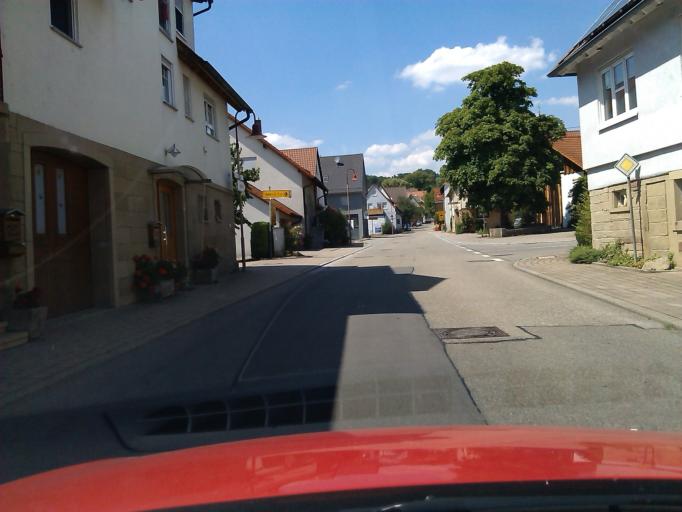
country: DE
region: Baden-Wuerttemberg
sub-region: Regierungsbezirk Stuttgart
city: Guglingen
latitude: 49.0959
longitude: 9.0257
